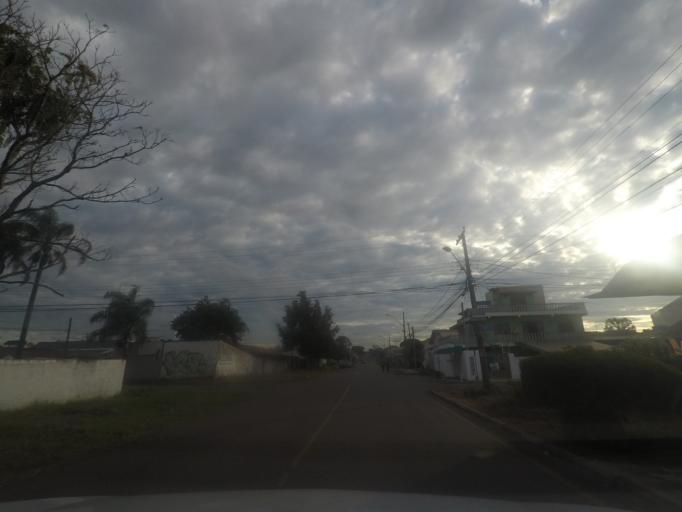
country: BR
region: Parana
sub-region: Pinhais
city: Pinhais
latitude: -25.4646
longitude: -49.2012
